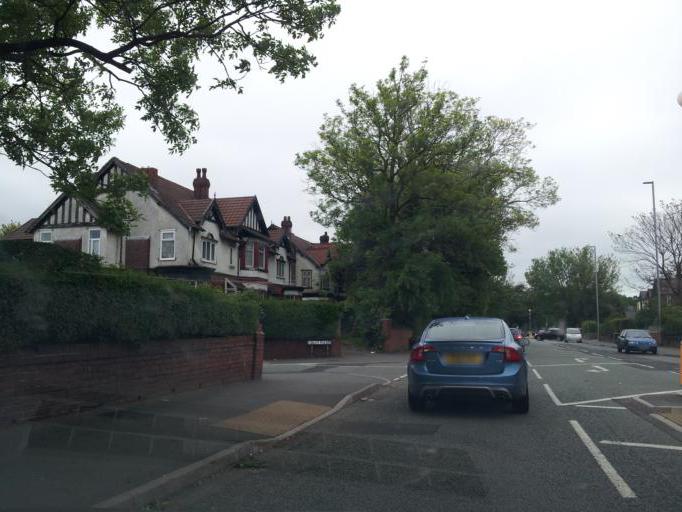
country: GB
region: England
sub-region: Manchester
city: Crumpsall
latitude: 53.5116
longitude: -2.2522
